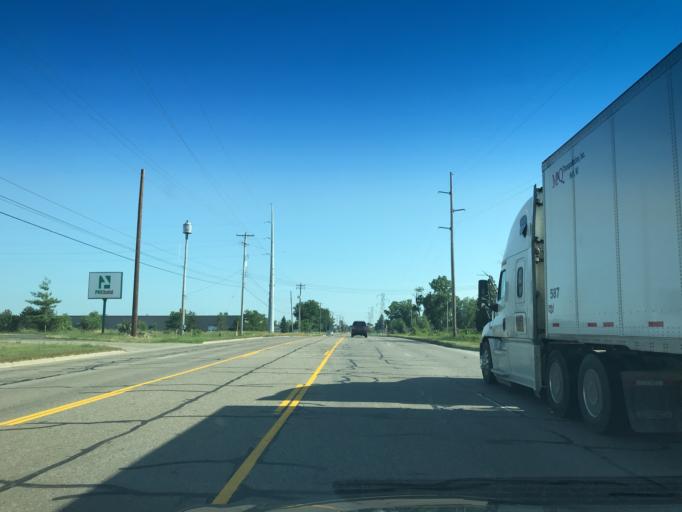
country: US
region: Michigan
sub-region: Eaton County
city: Waverly
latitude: 42.6963
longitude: -84.6424
